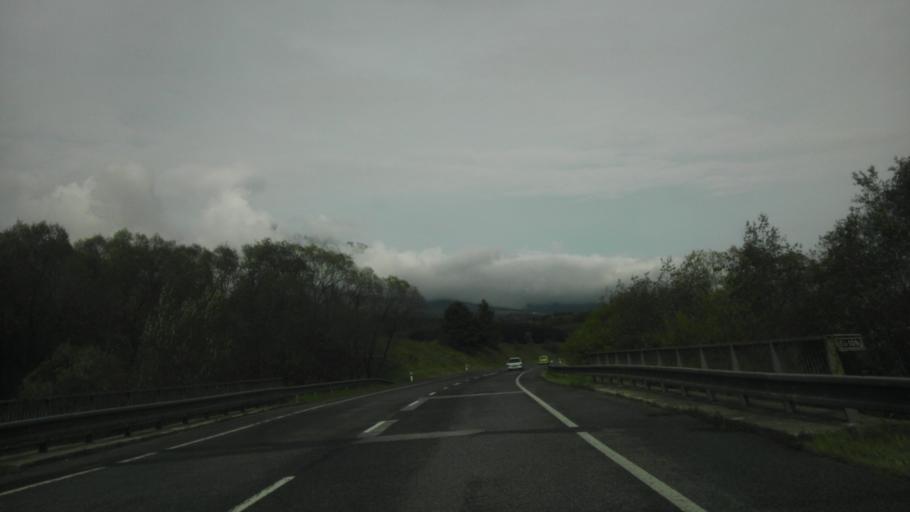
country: SK
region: Presovsky
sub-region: Okres Poprad
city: Nova Lesna
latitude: 49.1023
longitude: 20.2599
